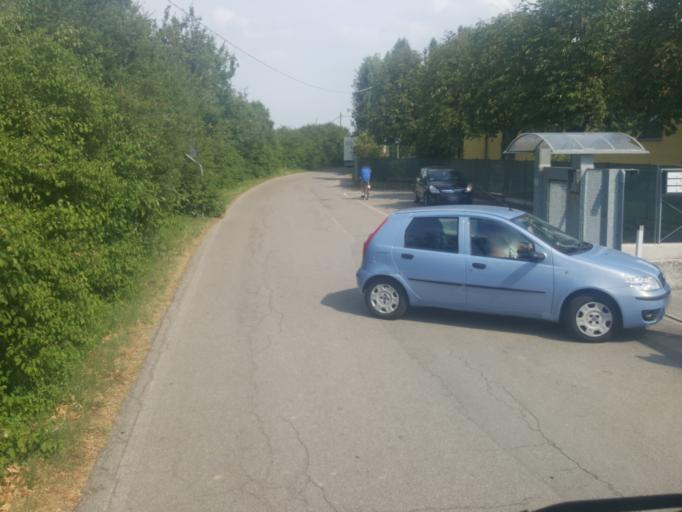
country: IT
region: Emilia-Romagna
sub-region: Provincia di Modena
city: Gaggio
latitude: 44.6374
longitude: 11.0057
